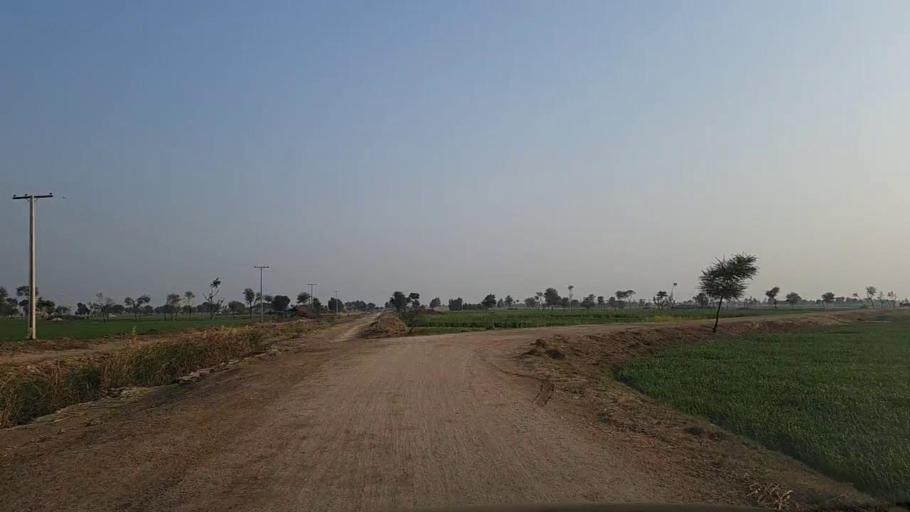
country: PK
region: Sindh
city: Daur
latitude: 26.3977
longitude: 68.3915
